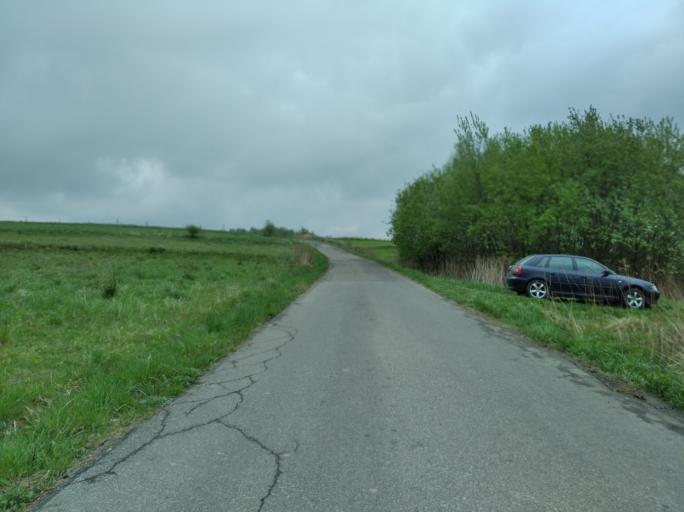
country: PL
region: Subcarpathian Voivodeship
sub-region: Powiat brzozowski
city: Golcowa
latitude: 49.7520
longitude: 22.0462
